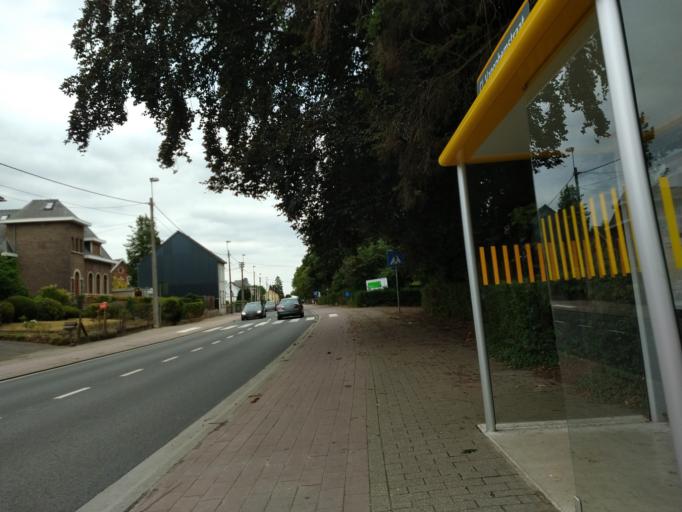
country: BE
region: Flanders
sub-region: Provincie Vlaams-Brabant
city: Overijse
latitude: 50.7777
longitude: 4.5231
